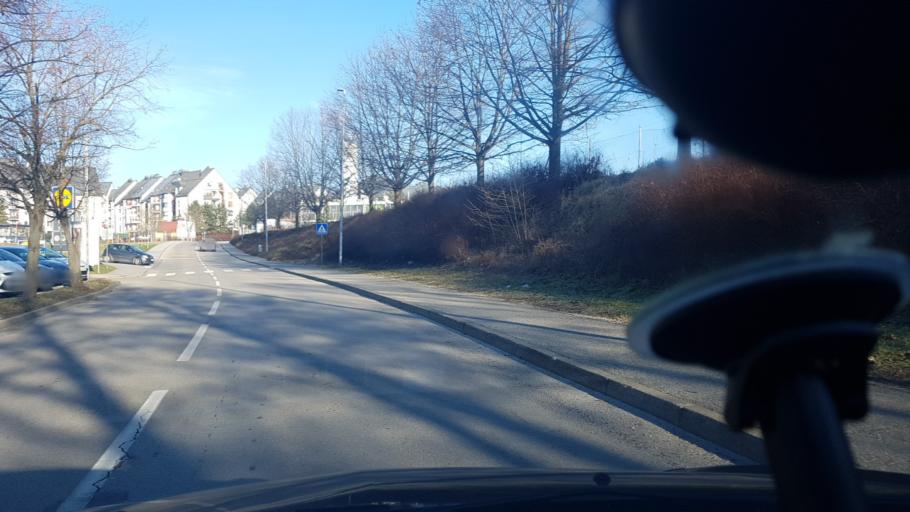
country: SI
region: Ptuj
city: Ptuj
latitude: 46.4268
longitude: 15.8673
